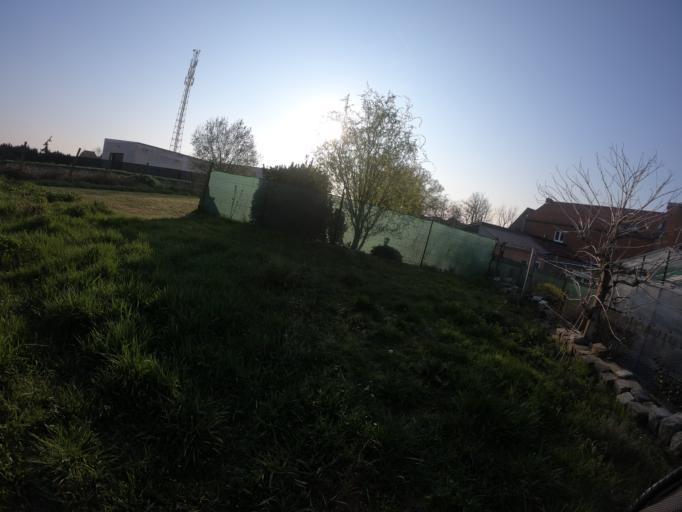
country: BE
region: Flanders
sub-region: Provincie Limburg
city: Borgloon
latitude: 50.8079
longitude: 5.2925
